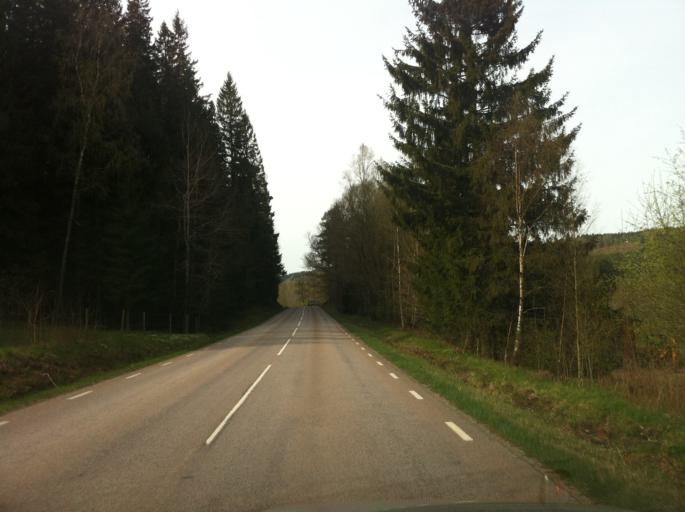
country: SE
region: Vaestra Goetaland
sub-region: Bollebygds Kommun
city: Bollebygd
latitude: 57.7048
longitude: 12.5816
